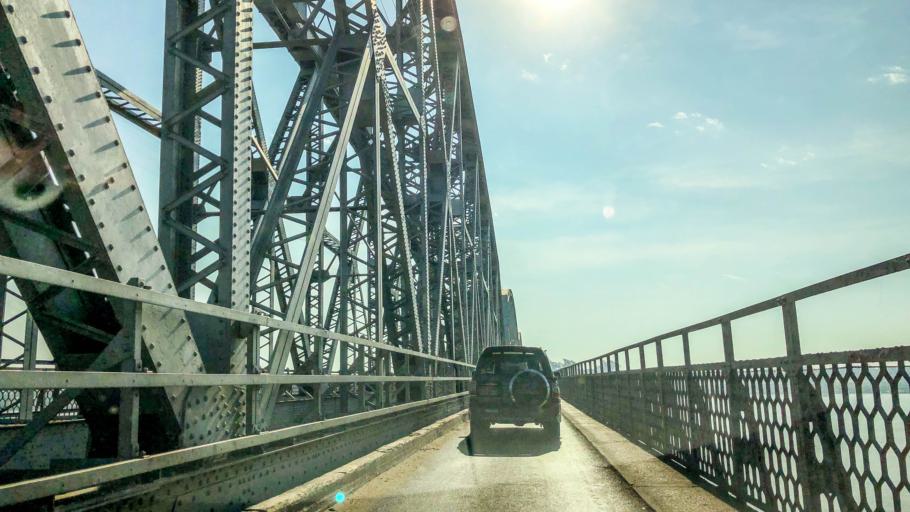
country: MM
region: Sagain
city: Sagaing
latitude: 21.8740
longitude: 95.9891
